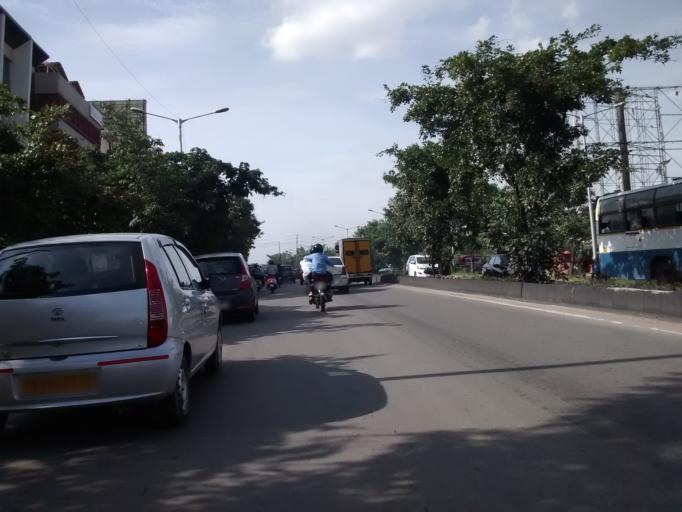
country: IN
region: Karnataka
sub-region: Bangalore Urban
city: Bangalore
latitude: 13.0041
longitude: 77.6631
